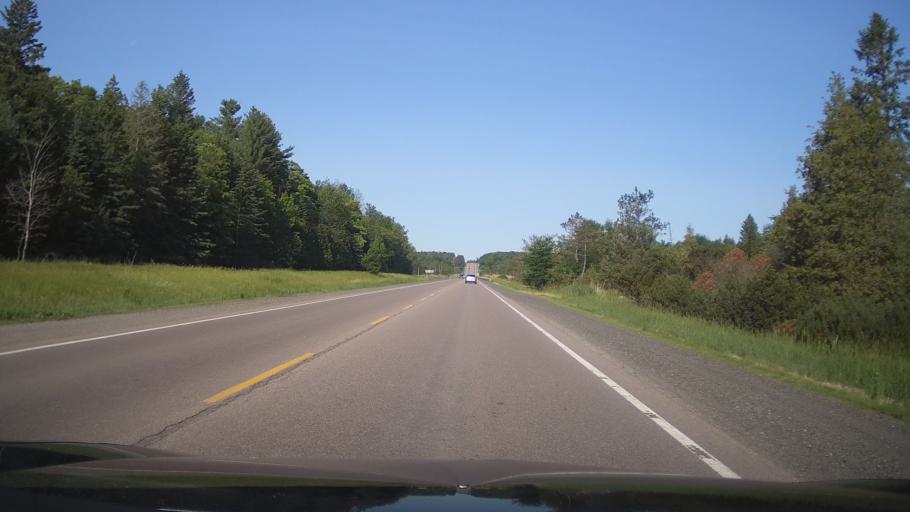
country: CA
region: Ontario
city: Quinte West
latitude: 44.4944
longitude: -77.6378
